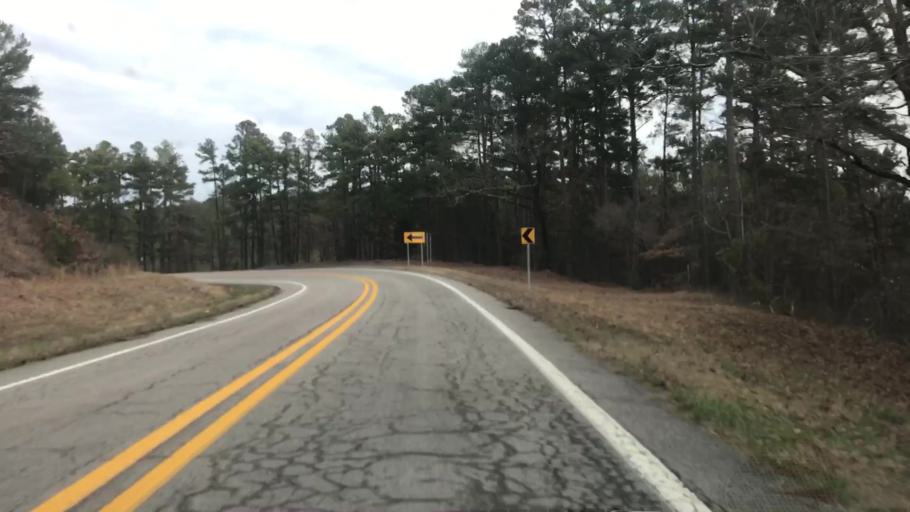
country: US
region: Arkansas
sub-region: Montgomery County
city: Mount Ida
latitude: 34.6745
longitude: -93.7850
